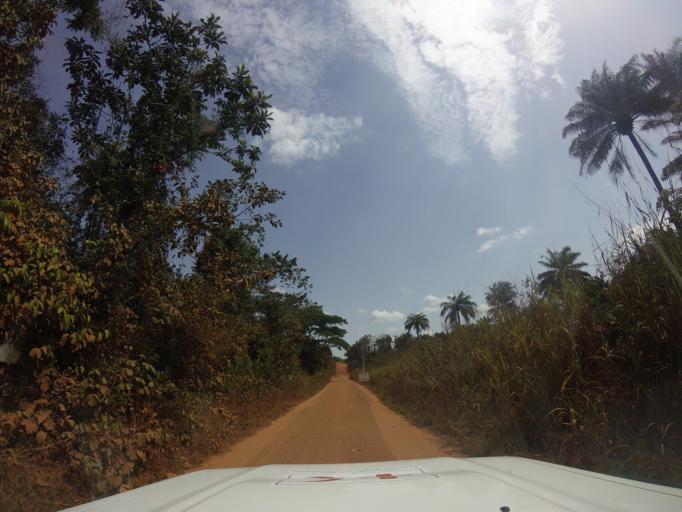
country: LR
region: Grand Cape Mount
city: Robertsport
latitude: 6.9897
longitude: -11.2990
